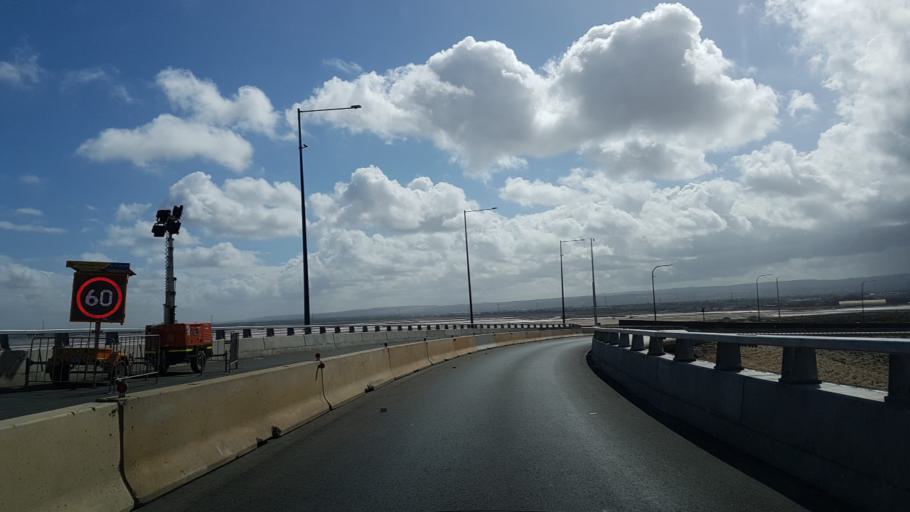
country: AU
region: South Australia
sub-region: Port Adelaide Enfield
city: Blair Athol
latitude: -34.8290
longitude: 138.5632
